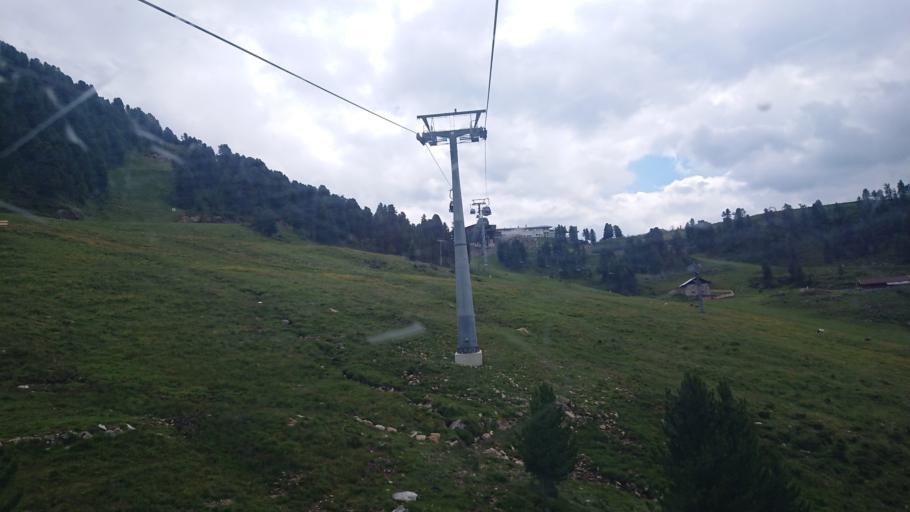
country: AT
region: Tyrol
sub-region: Politischer Bezirk Imst
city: Oetz
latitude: 47.2163
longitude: 10.9320
